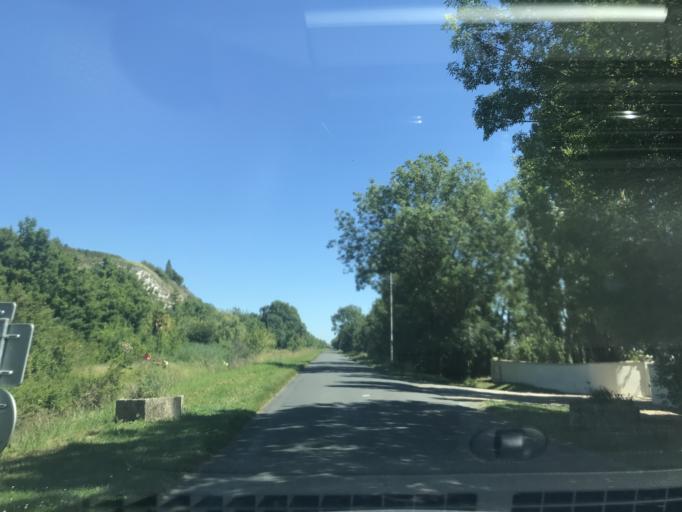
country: FR
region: Poitou-Charentes
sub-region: Departement de la Charente-Maritime
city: Mortagne-sur-Gironde
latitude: 45.4763
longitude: -0.7904
